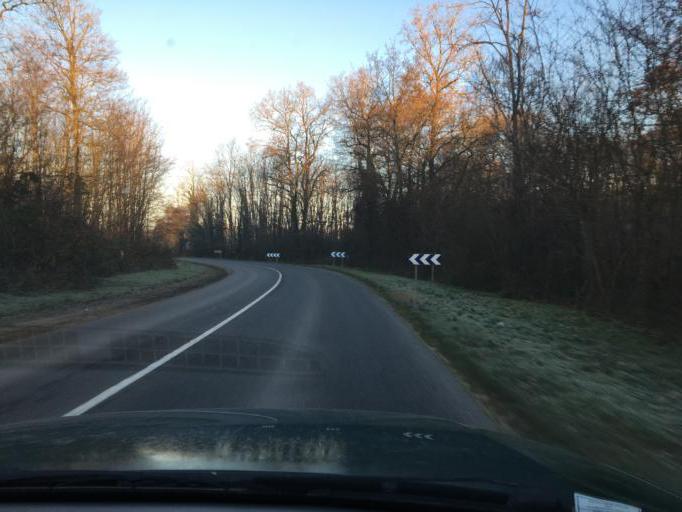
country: FR
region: Centre
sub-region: Departement du Loiret
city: Saran
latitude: 47.9678
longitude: 1.8674
